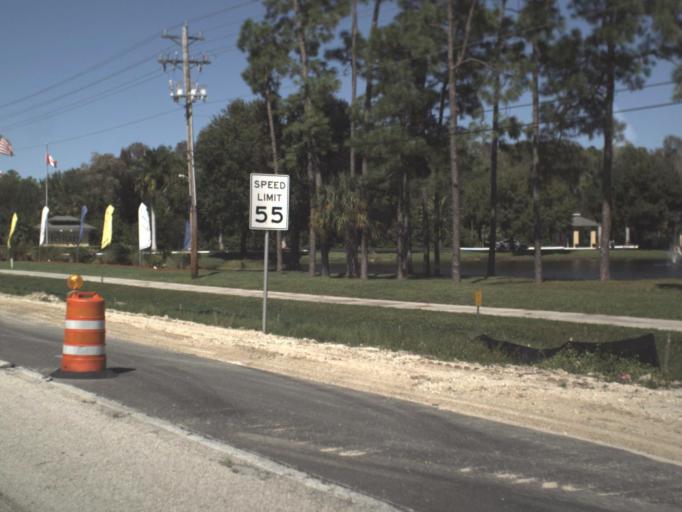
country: US
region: Florida
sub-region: Lee County
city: Suncoast Estates
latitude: 26.7272
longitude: -81.9074
